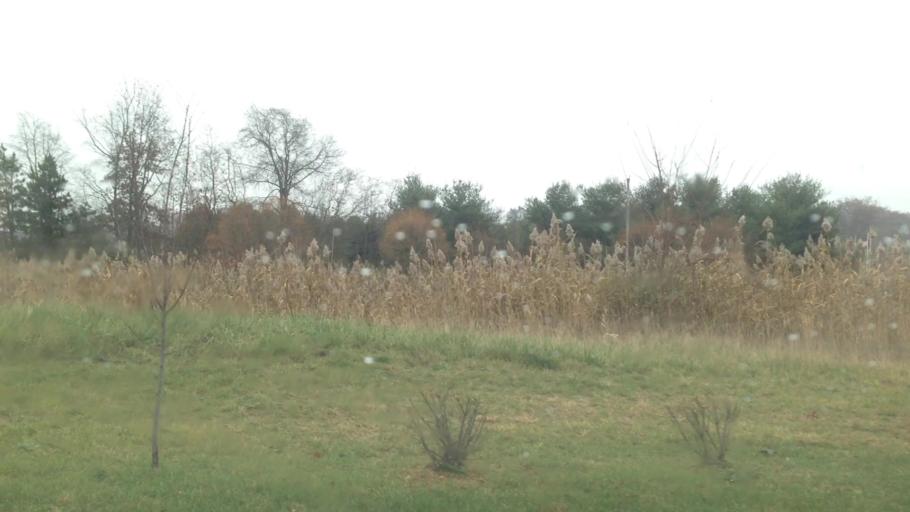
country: US
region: Indiana
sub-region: Saint Joseph County
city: Mishawaka
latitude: 41.7110
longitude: -86.1665
